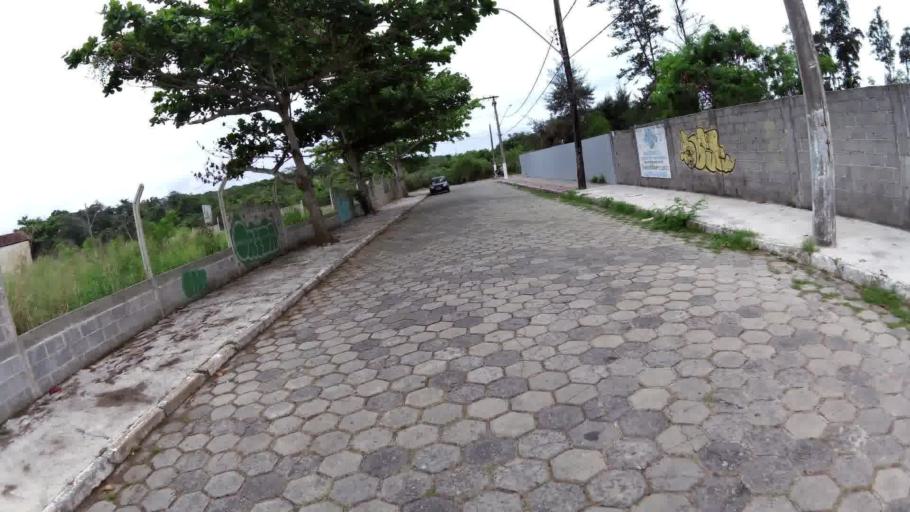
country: BR
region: Espirito Santo
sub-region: Guarapari
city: Guarapari
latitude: -20.6522
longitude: -40.4737
